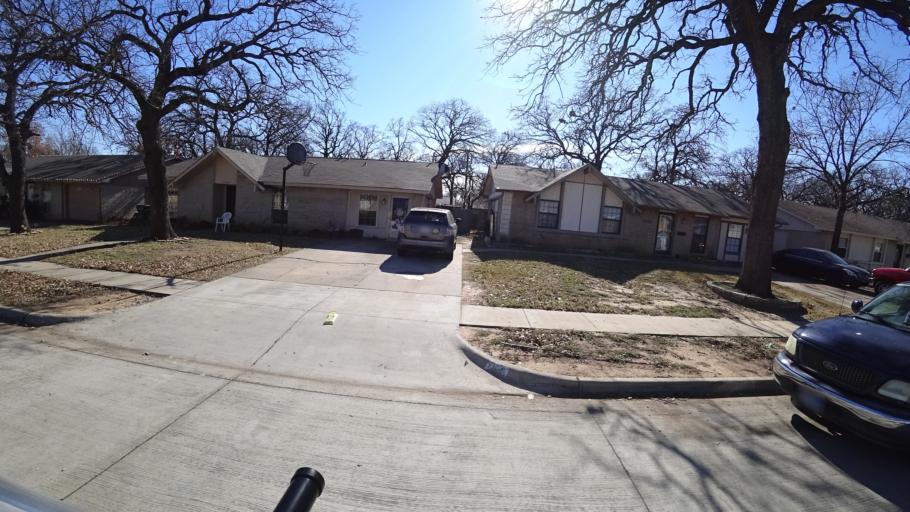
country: US
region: Texas
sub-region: Denton County
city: Lewisville
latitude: 33.0331
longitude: -97.0230
